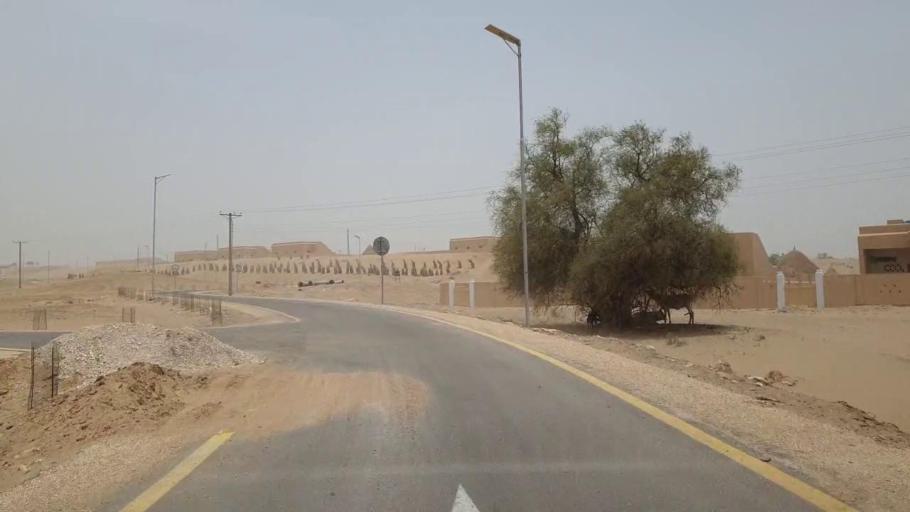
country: PK
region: Sindh
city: Islamkot
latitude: 24.7228
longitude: 70.3241
